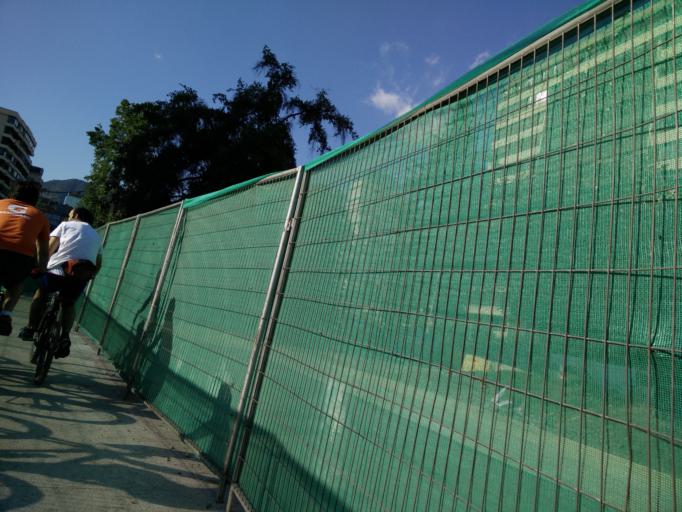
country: CL
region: Santiago Metropolitan
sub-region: Provincia de Santiago
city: Villa Presidente Frei, Nunoa, Santiago, Chile
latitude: -33.4033
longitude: -70.5866
